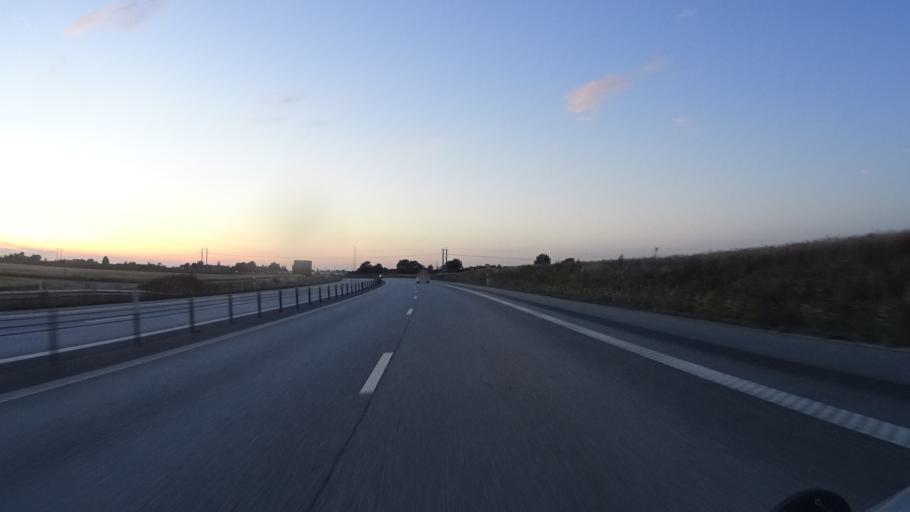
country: SE
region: Skane
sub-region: Trelleborgs Kommun
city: Skare
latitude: 55.4166
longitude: 13.0631
